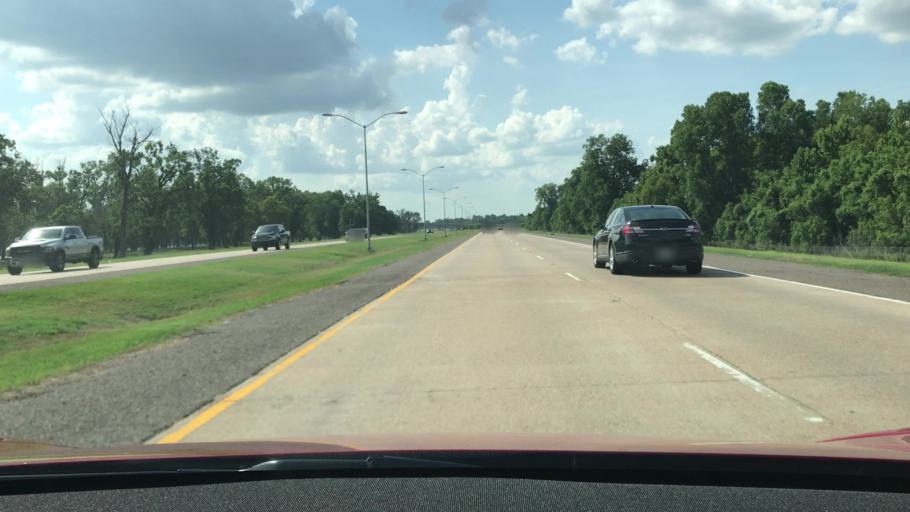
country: US
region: Louisiana
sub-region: Bossier Parish
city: Bossier City
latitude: 32.4855
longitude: -93.6871
